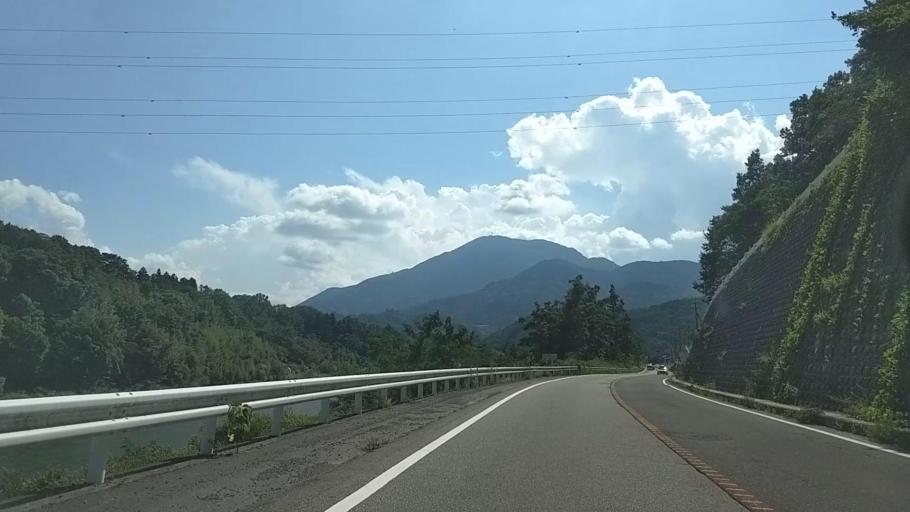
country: JP
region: Yamanashi
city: Ryuo
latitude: 35.4447
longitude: 138.4407
